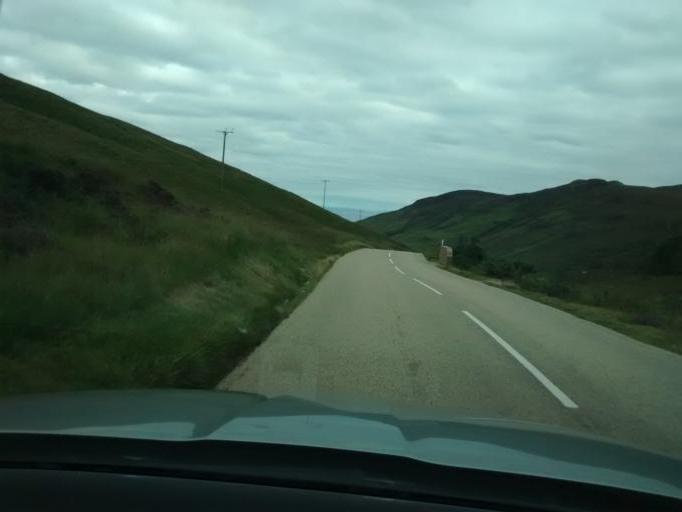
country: GB
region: Scotland
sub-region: North Ayrshire
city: Isle of Arran
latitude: 55.6784
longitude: -5.2141
